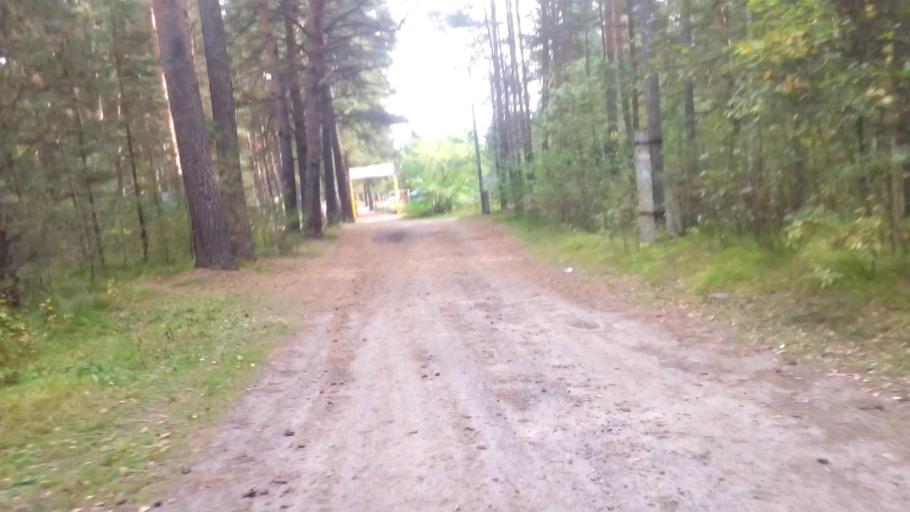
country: RU
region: Altai Krai
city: Yuzhnyy
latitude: 53.3103
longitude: 83.6930
